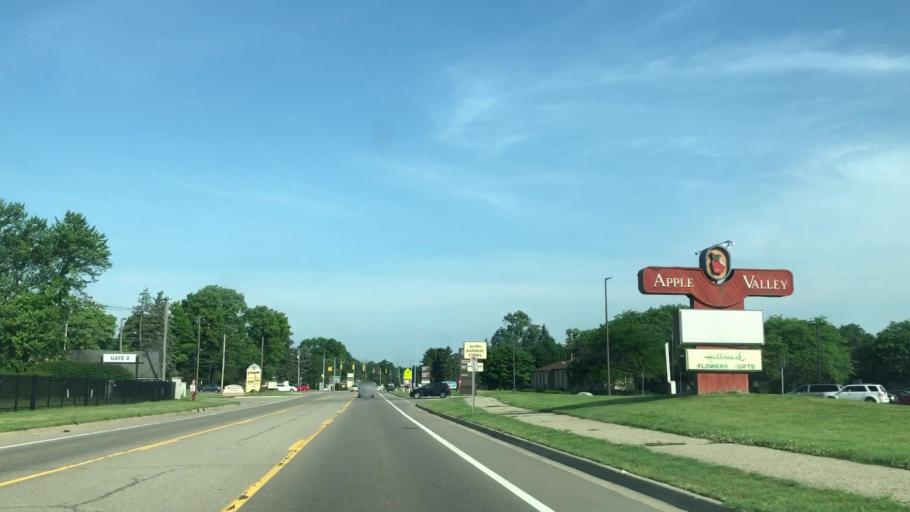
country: US
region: Michigan
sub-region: Berrien County
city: Berrien Springs
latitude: 41.9544
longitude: -86.3545
